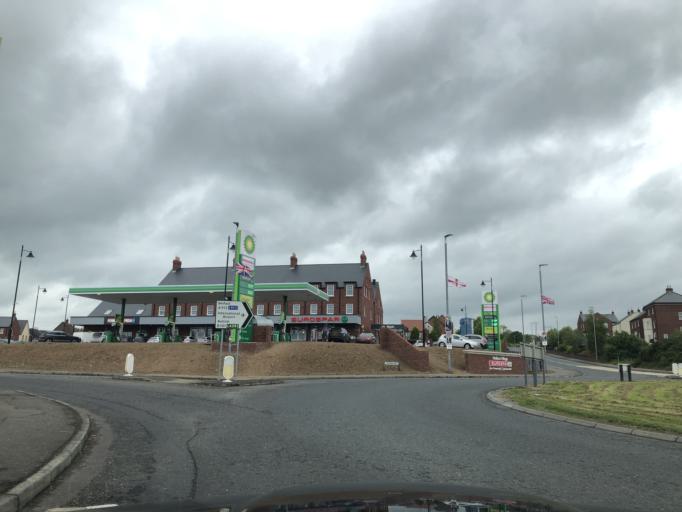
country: GB
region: Northern Ireland
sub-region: Lisburn District
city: Lisburn
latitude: 54.5284
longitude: -6.0728
